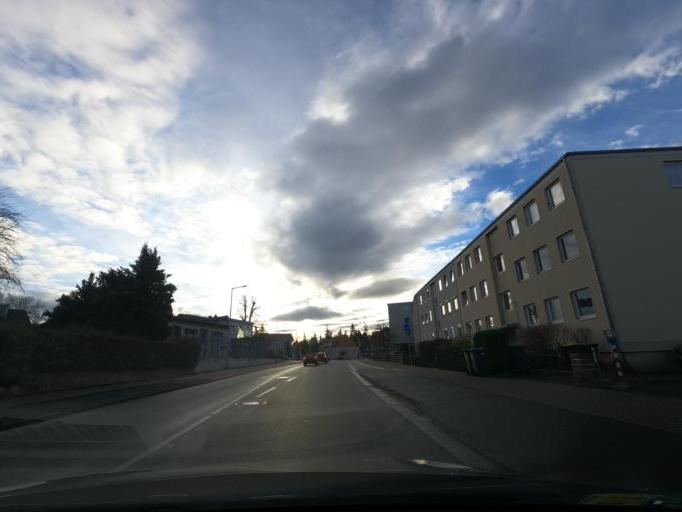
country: DE
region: Lower Saxony
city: Wolfenbuettel
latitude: 52.1657
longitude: 10.5493
